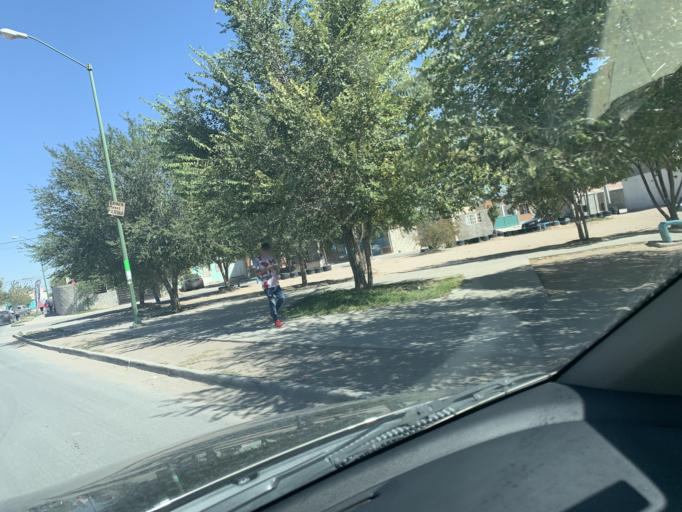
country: US
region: Texas
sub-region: El Paso County
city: Socorro Mission Number 1 Colonia
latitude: 31.5971
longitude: -106.3601
